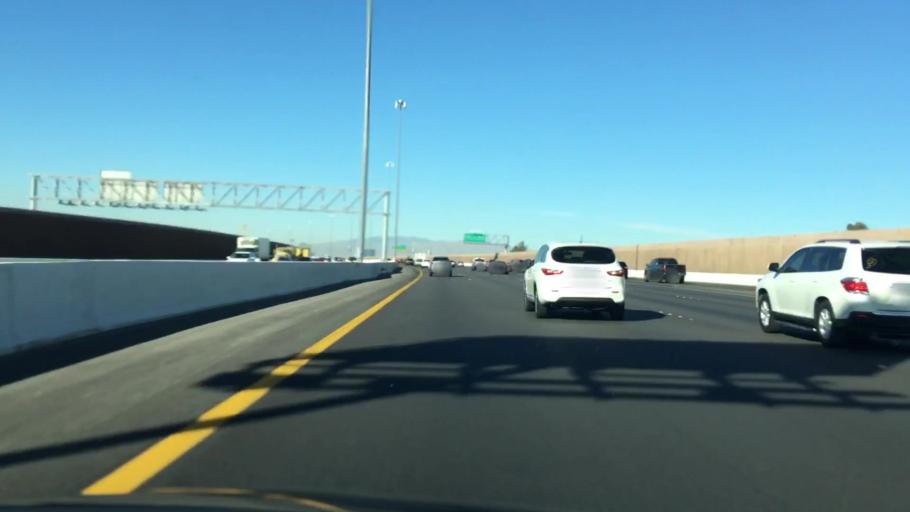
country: US
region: Nevada
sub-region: Clark County
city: Paradise
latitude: 36.0452
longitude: -115.1341
